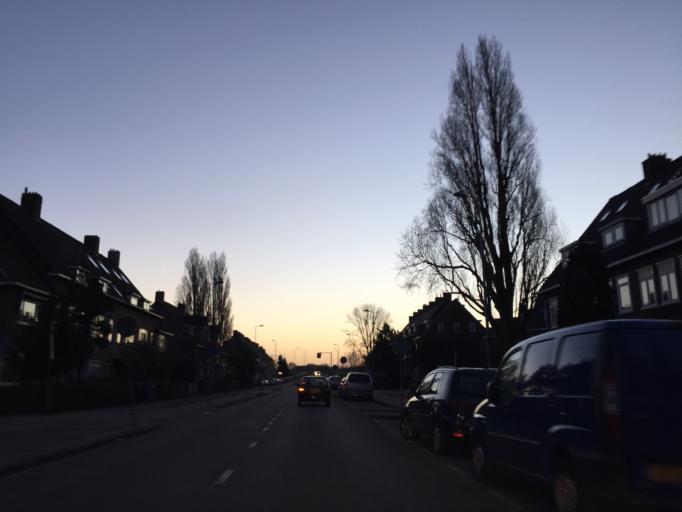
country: NL
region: South Holland
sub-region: Gemeente Rotterdam
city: Rotterdam
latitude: 51.9438
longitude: 4.4724
